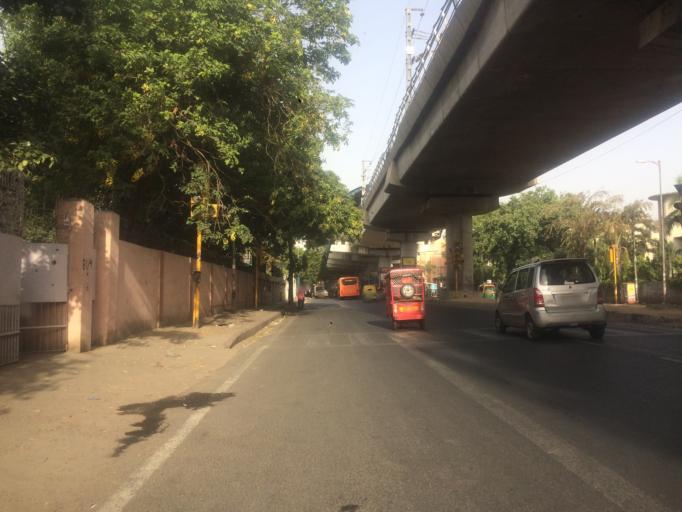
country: IN
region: NCT
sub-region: Central Delhi
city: Karol Bagh
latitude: 28.6443
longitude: 77.1904
